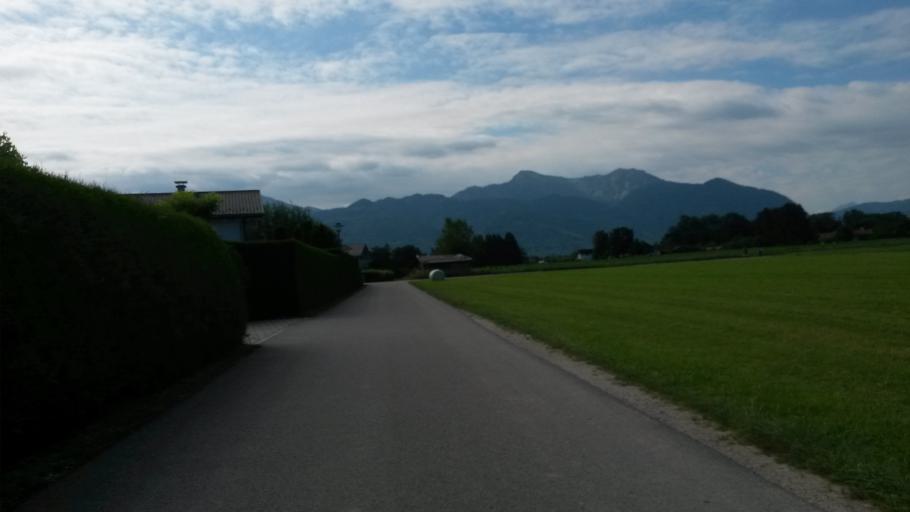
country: DE
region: Bavaria
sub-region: Upper Bavaria
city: Ubersee
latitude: 47.8315
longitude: 12.4887
